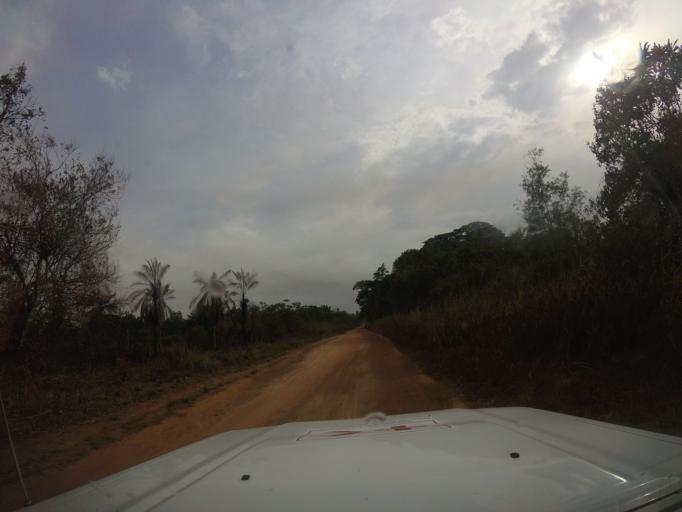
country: LR
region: Grand Cape Mount
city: Robertsport
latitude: 6.9765
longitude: -11.3071
